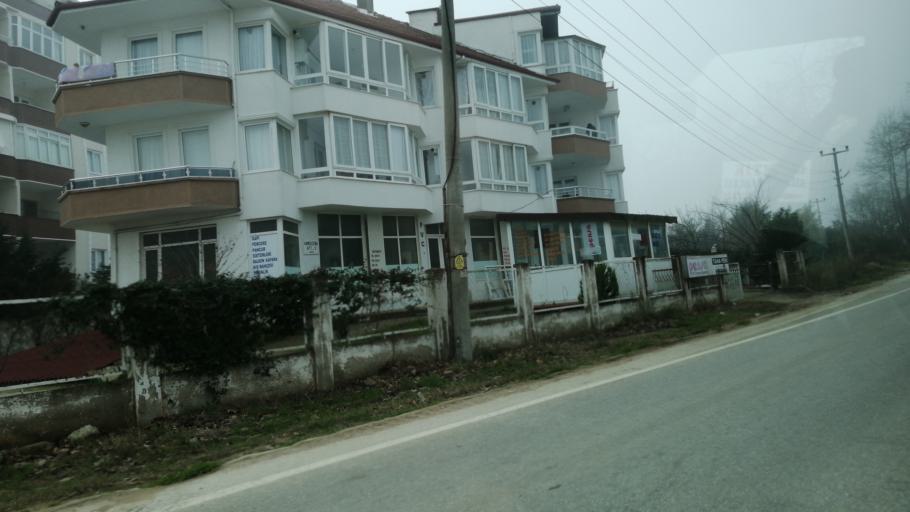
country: TR
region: Yalova
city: Cinarcik
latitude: 40.6417
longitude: 29.0849
